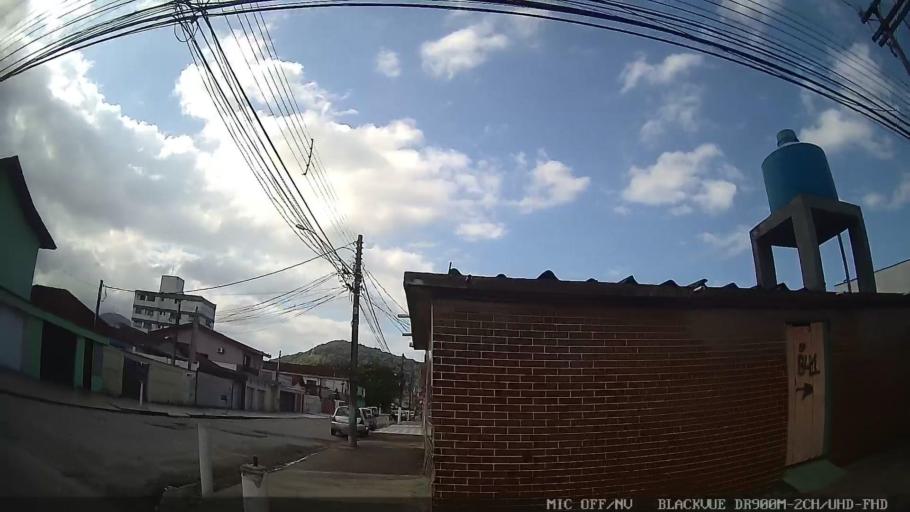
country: BR
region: Sao Paulo
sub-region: Guaruja
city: Guaruja
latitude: -23.9935
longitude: -46.2793
